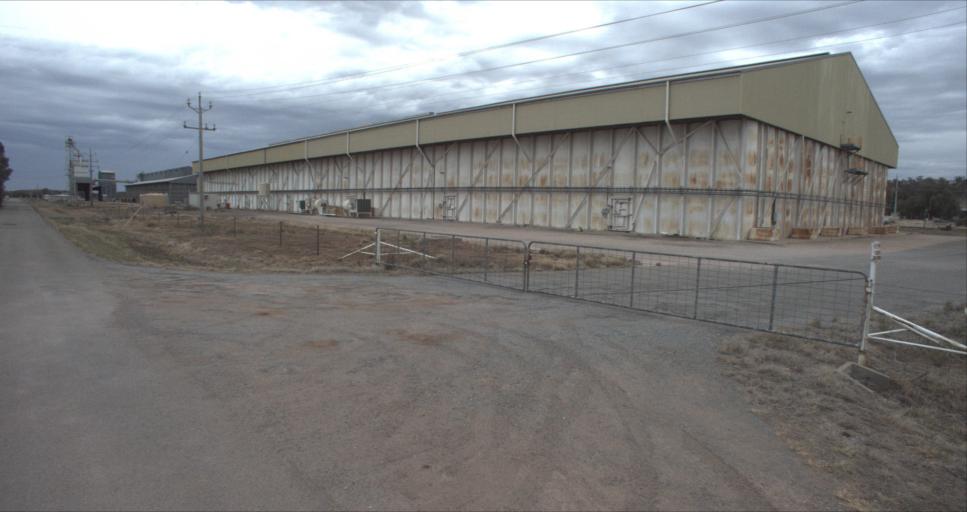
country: AU
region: New South Wales
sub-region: Leeton
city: Leeton
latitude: -34.4286
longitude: 146.3075
